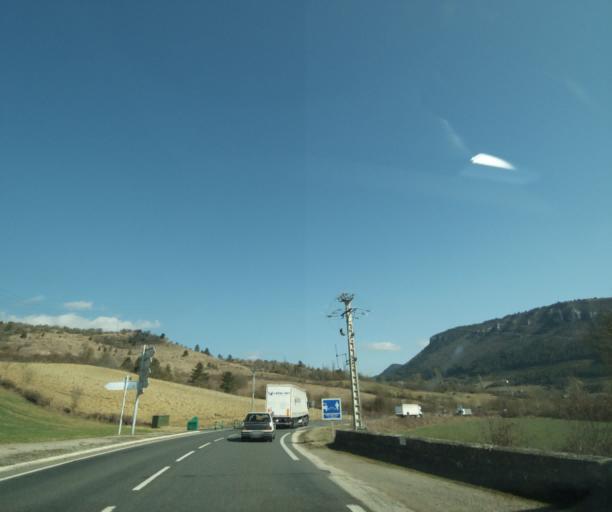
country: FR
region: Languedoc-Roussillon
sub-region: Departement de la Lozere
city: Chanac
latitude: 44.5005
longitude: 3.3990
